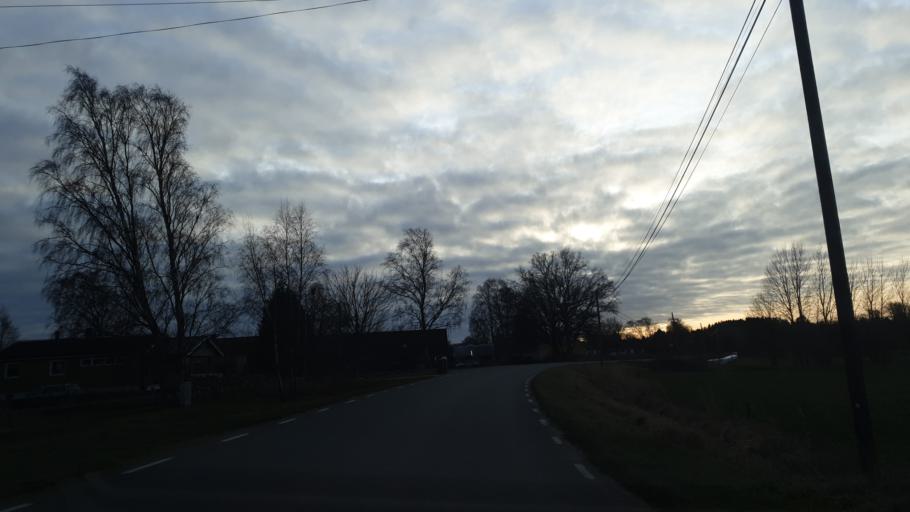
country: SE
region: Blekinge
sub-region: Karlskrona Kommun
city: Jaemjoe
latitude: 56.1847
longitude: 15.9418
